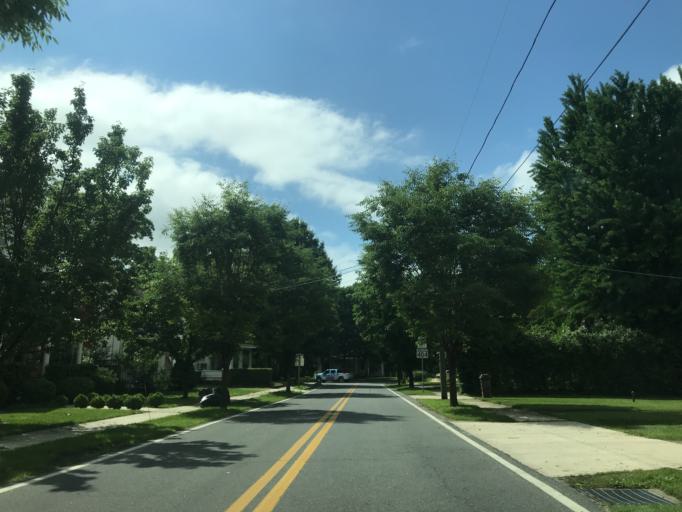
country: US
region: Maryland
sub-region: Caroline County
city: Ridgely
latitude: 38.9185
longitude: -75.9537
